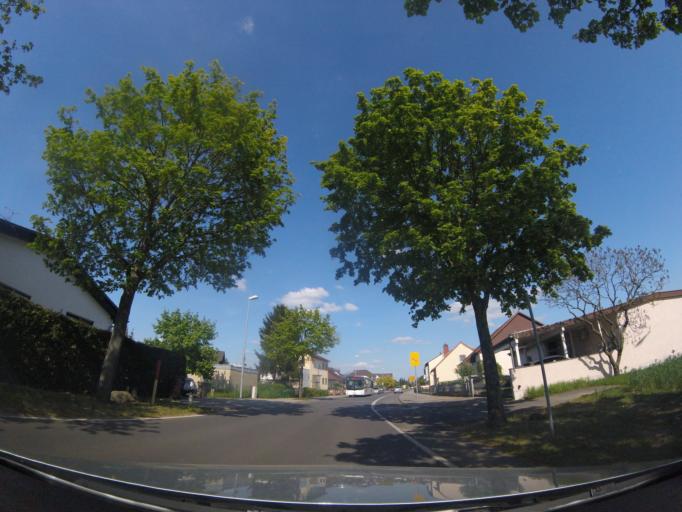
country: DE
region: Hesse
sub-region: Regierungsbezirk Darmstadt
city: Buttelborn
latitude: 49.9239
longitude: 8.5391
